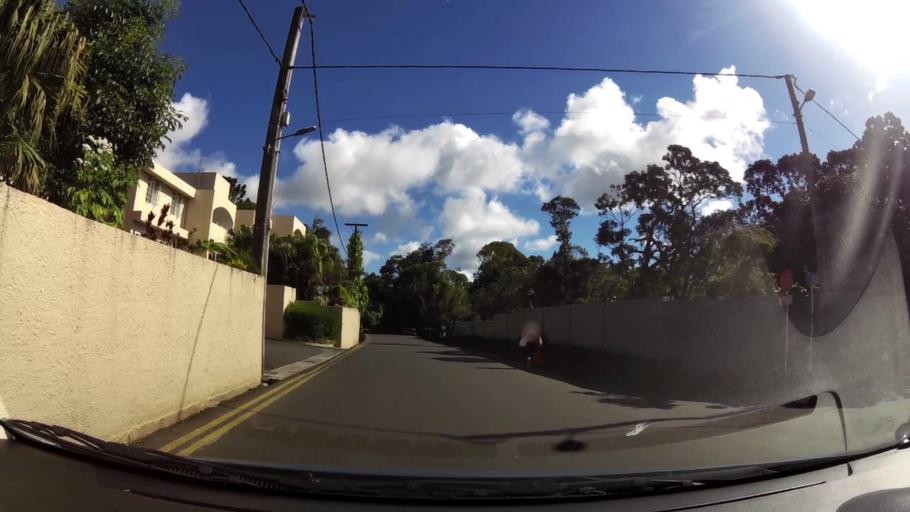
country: MU
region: Plaines Wilhems
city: Curepipe
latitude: -20.3235
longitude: 57.5235
